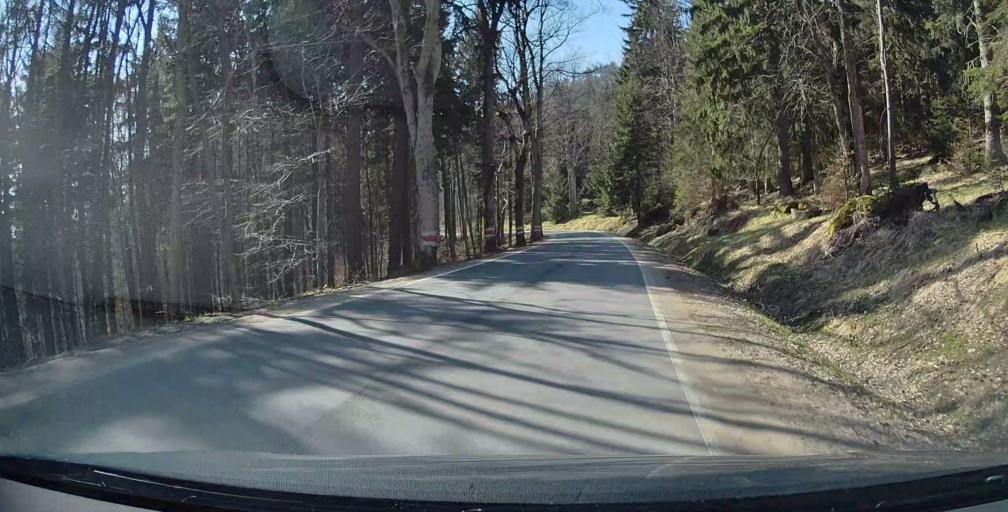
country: CZ
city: Machov
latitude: 50.4636
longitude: 16.3256
